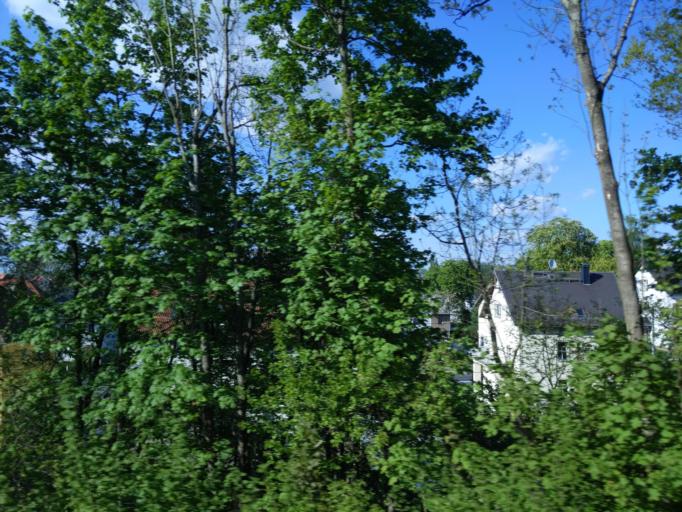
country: DE
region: Saxony
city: Ottendorf-Okrilla
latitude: 51.1255
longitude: 13.8496
